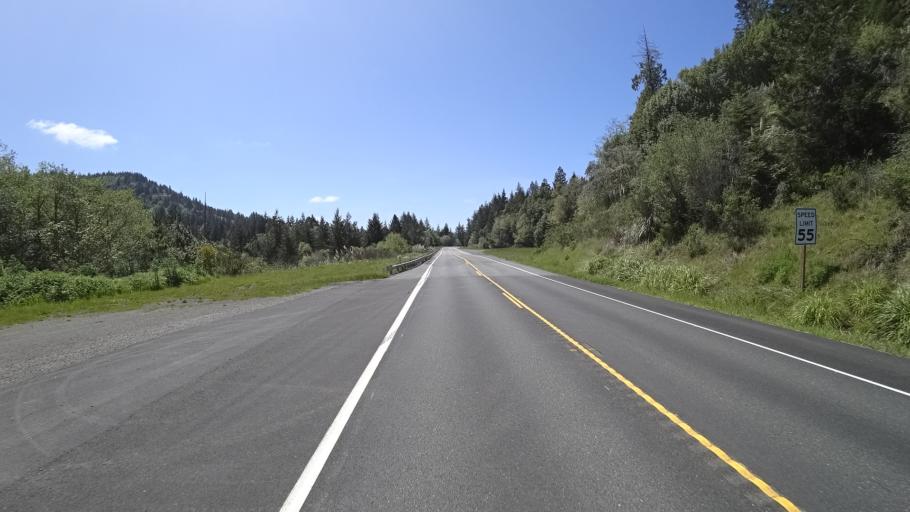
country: US
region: California
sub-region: Humboldt County
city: Blue Lake
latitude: 40.8929
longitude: -123.9360
